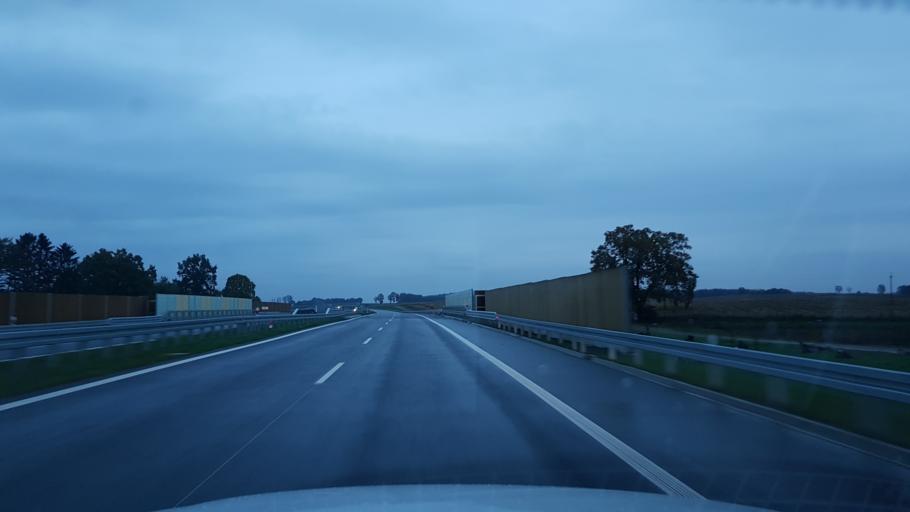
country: PL
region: West Pomeranian Voivodeship
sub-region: Powiat gryficki
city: Brojce
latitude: 53.8961
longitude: 15.3829
